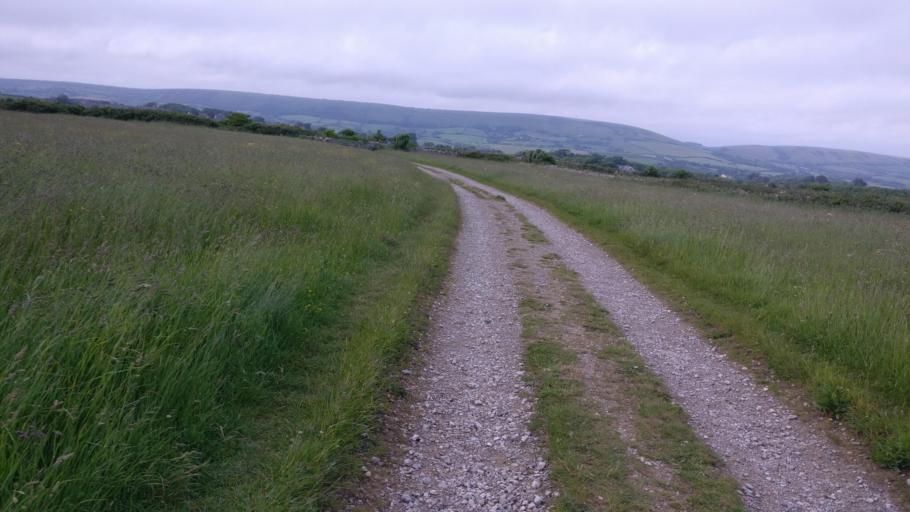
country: GB
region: England
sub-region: Dorset
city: Swanage
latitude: 50.6006
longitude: -2.0082
